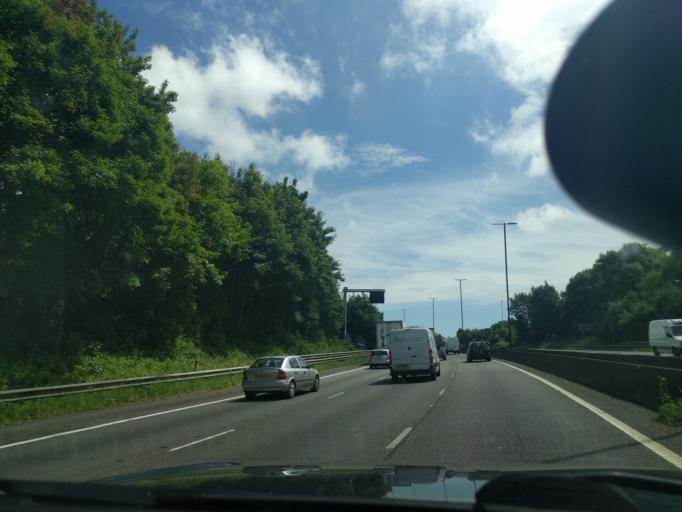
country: GB
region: Wales
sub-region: Newport
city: Caerleon
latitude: 51.5951
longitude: -2.9627
